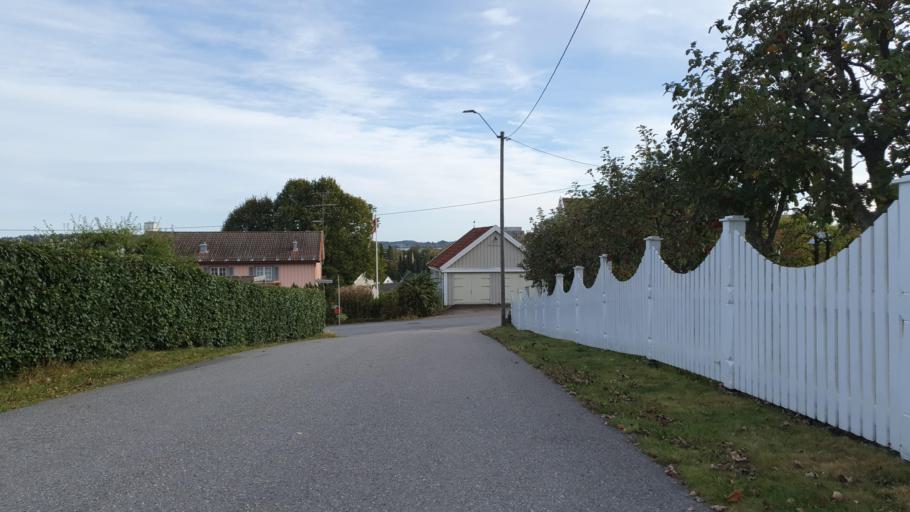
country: NO
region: Vestfold
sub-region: Tonsberg
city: Tonsberg
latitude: 59.2787
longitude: 10.4187
